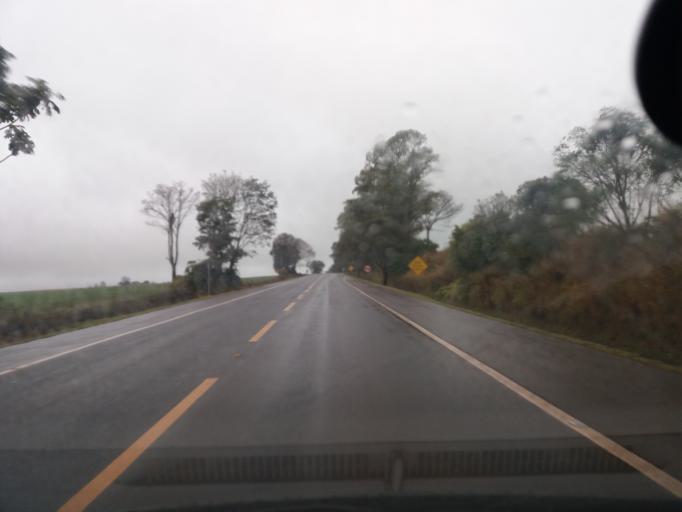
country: BR
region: Parana
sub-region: Campo Mourao
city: Campo Mourao
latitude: -24.3171
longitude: -52.6233
